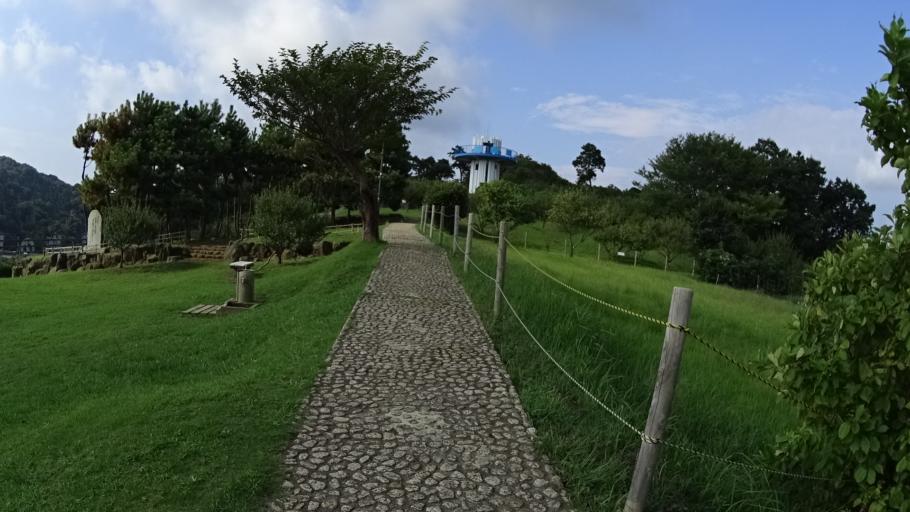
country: JP
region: Kanagawa
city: Yokosuka
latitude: 35.2846
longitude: 139.6305
